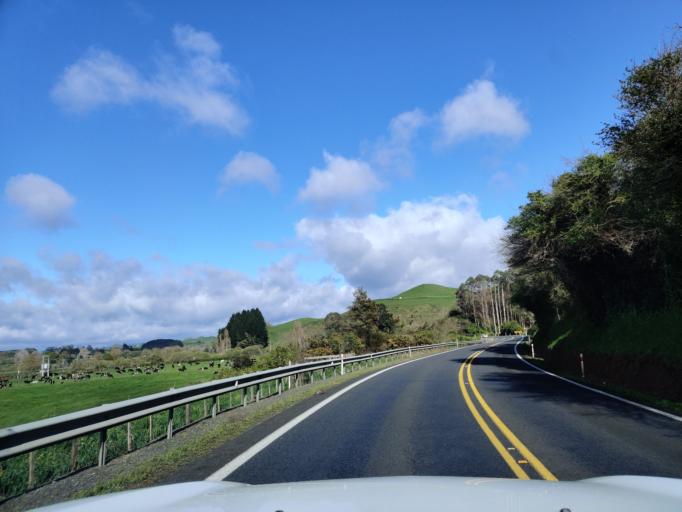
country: NZ
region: Waikato
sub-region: Otorohanga District
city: Otorohanga
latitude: -38.0437
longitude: 175.1776
